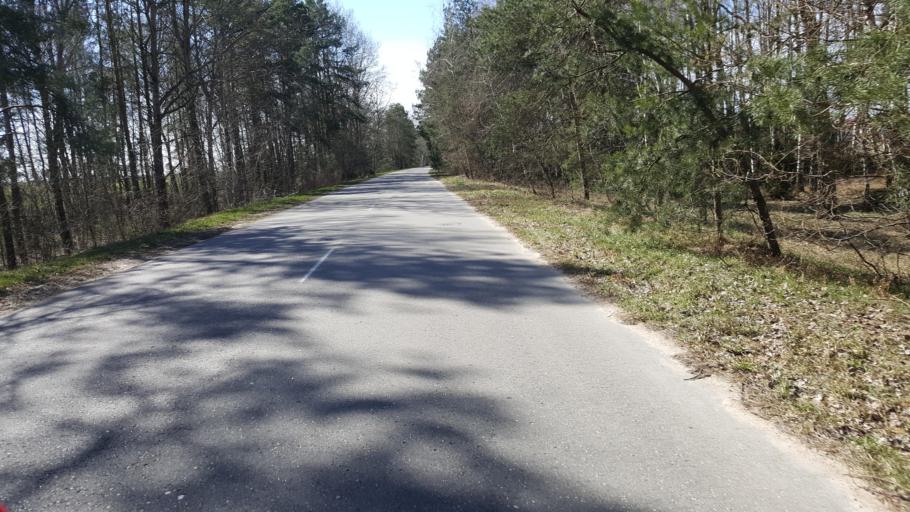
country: BY
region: Brest
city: Charnawchytsy
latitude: 52.2893
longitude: 23.7848
